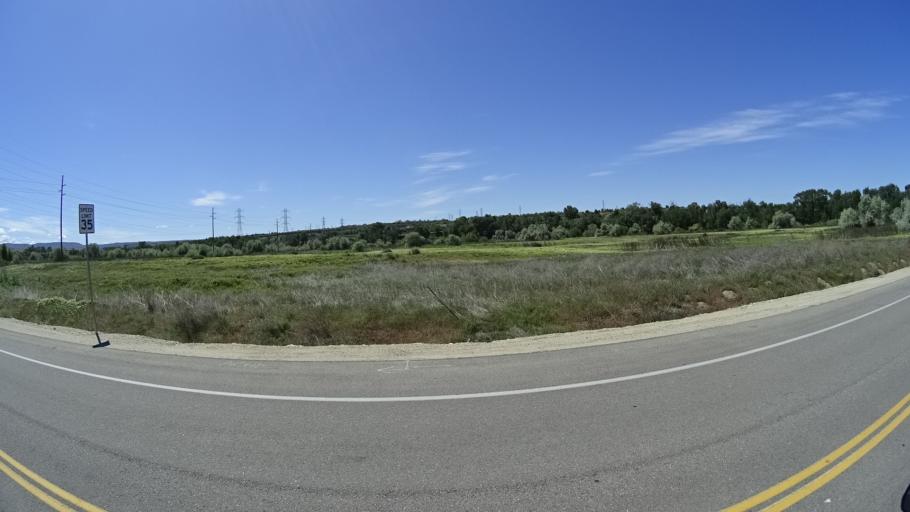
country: US
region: Idaho
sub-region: Ada County
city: Boise
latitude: 43.5666
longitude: -116.1275
